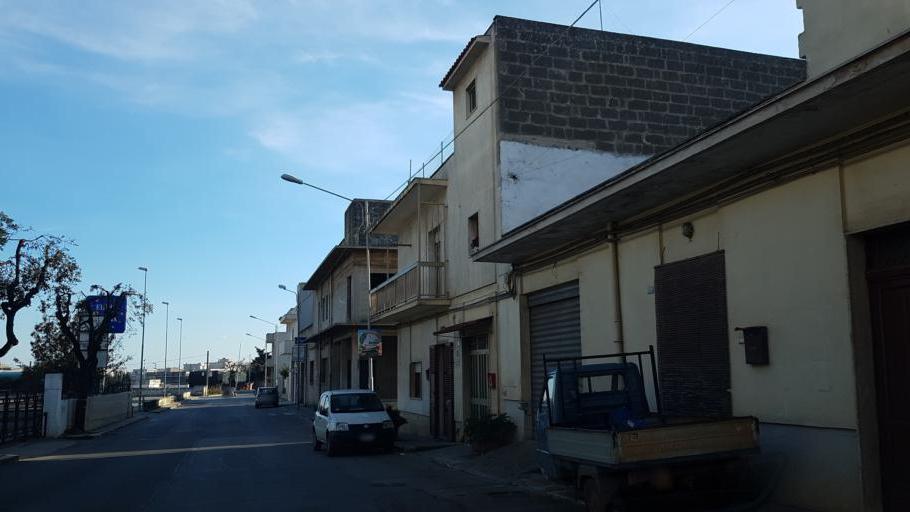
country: IT
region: Apulia
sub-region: Provincia di Brindisi
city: Carovigno
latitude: 40.7073
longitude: 17.6631
